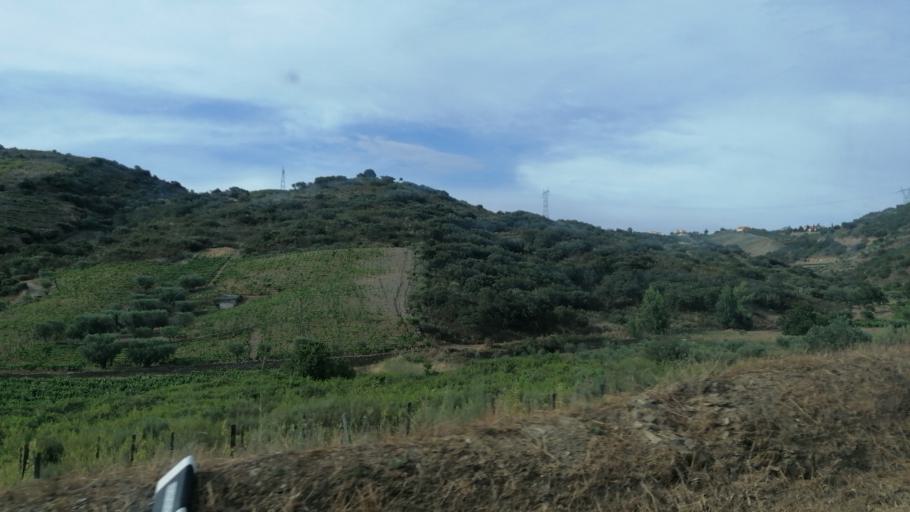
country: PT
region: Viseu
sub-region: Sao Joao da Pesqueira
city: Sao Joao da Pesqueira
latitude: 41.0868
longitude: -7.3842
